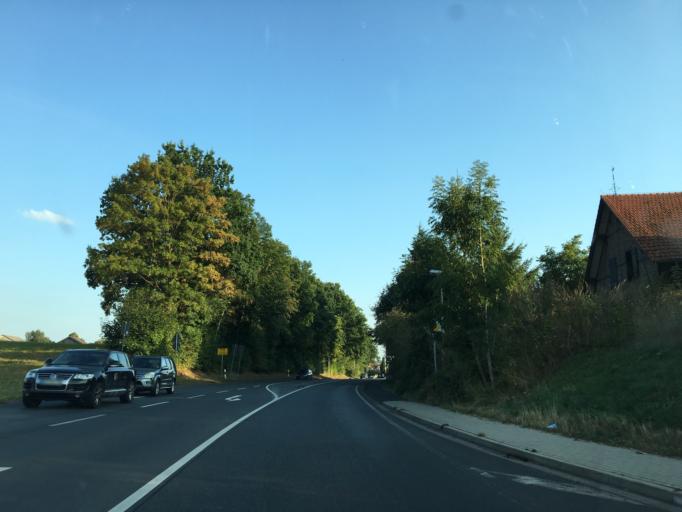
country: DE
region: Hesse
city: Wetter
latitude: 50.9089
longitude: 8.7240
